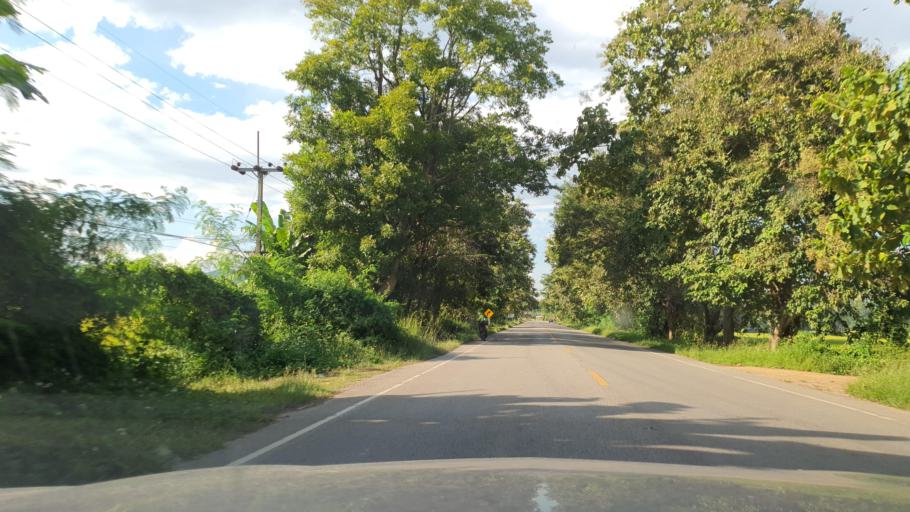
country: TH
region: Phayao
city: Phayao
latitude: 19.1422
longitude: 99.8349
